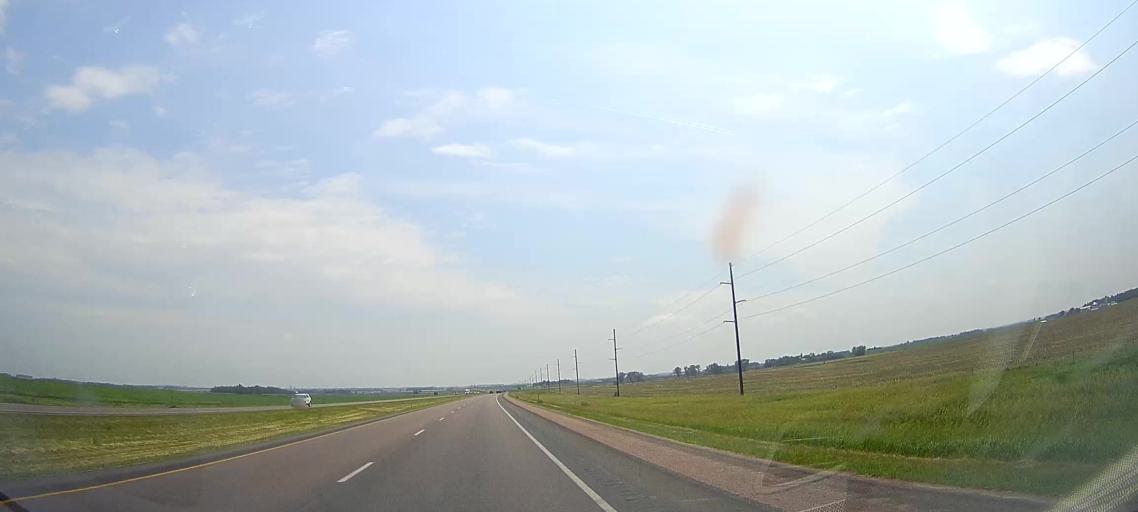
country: US
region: South Dakota
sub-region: Union County
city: Beresford
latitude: 43.1543
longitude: -96.7959
